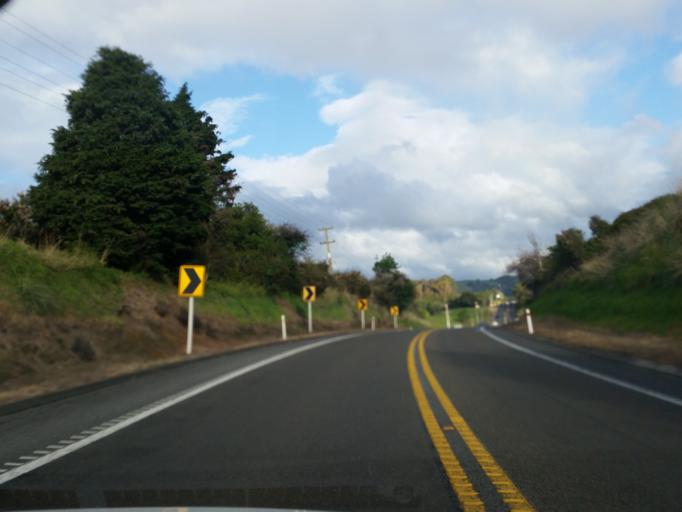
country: NZ
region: Bay of Plenty
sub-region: Tauranga City
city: Tauranga
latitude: -37.6698
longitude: 176.0211
